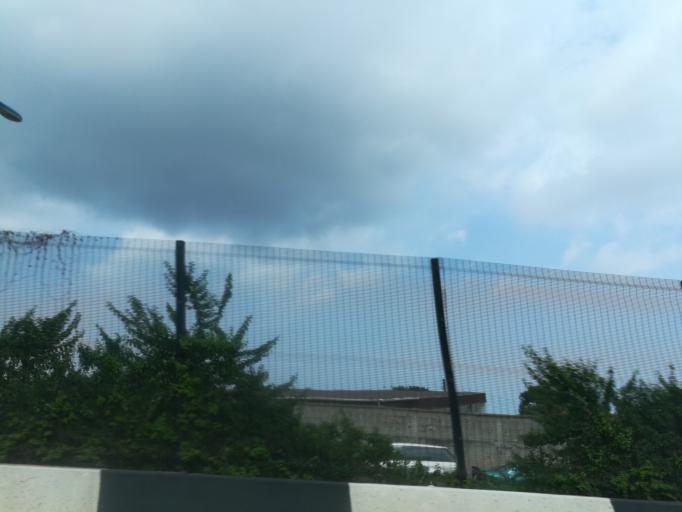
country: NG
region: Lagos
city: Ojota
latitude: 6.5613
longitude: 3.3955
